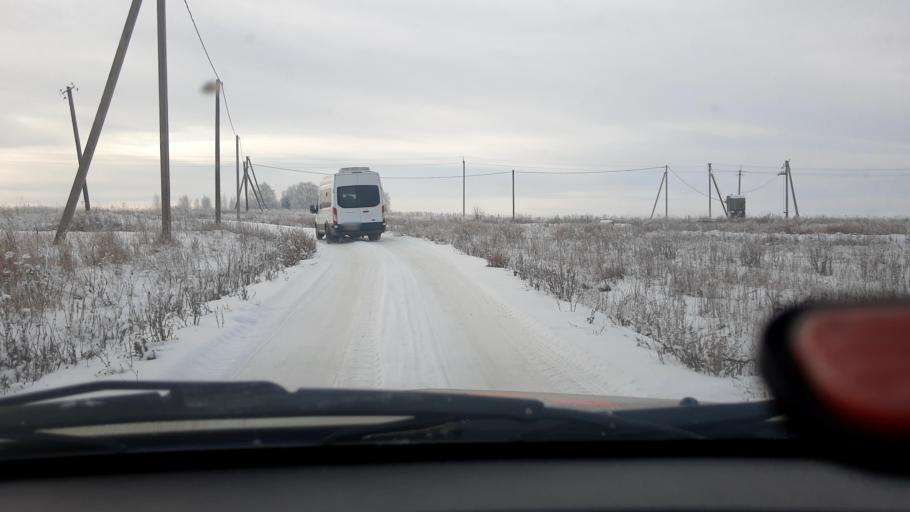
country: RU
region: Bashkortostan
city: Tolbazy
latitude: 54.3553
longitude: 55.8429
